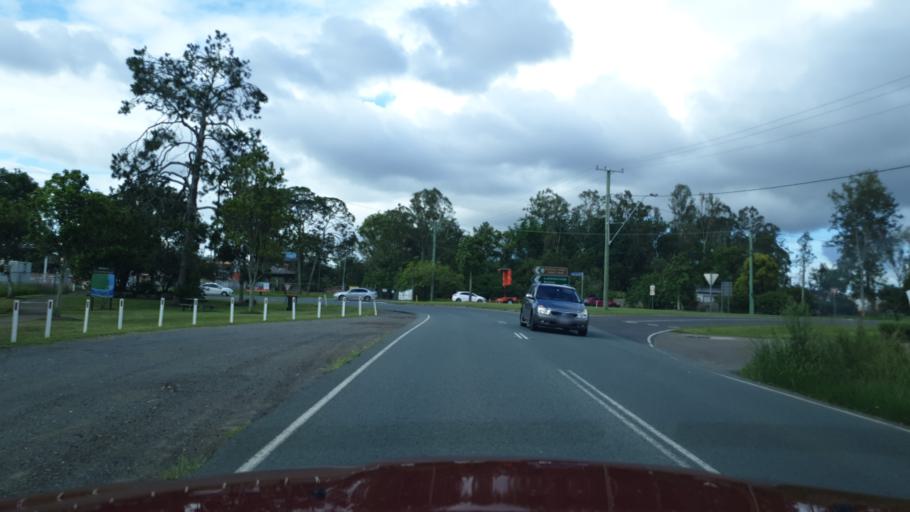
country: AU
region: Queensland
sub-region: Sunshine Coast
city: Little Mountain
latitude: -26.8102
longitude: 152.9665
